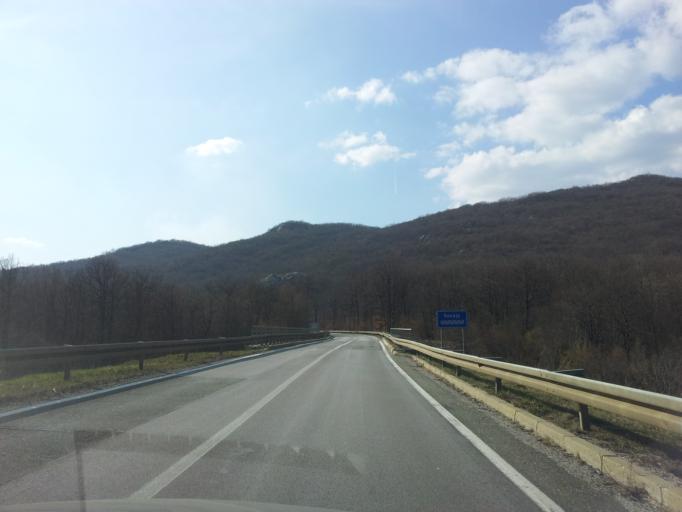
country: HR
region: Zadarska
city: Gracac
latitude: 44.4662
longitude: 15.7008
